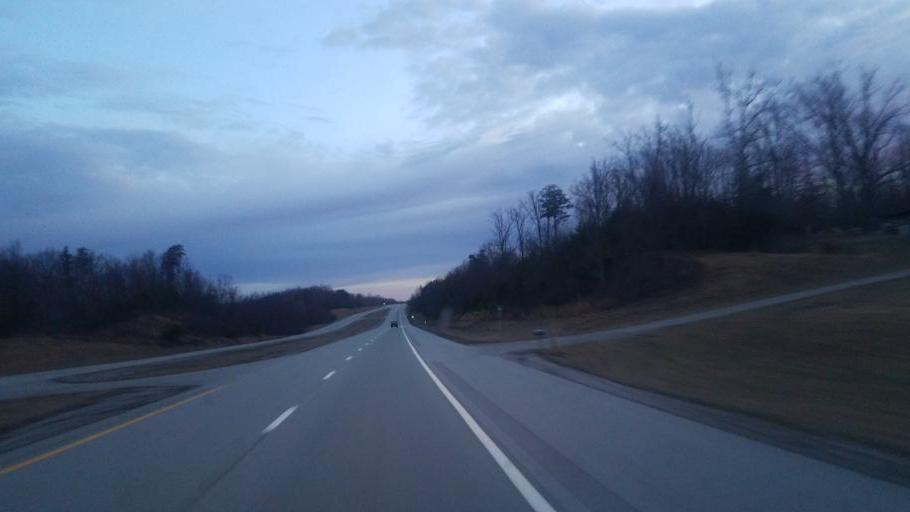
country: US
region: Tennessee
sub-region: Van Buren County
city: Spencer
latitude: 35.7163
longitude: -85.4717
